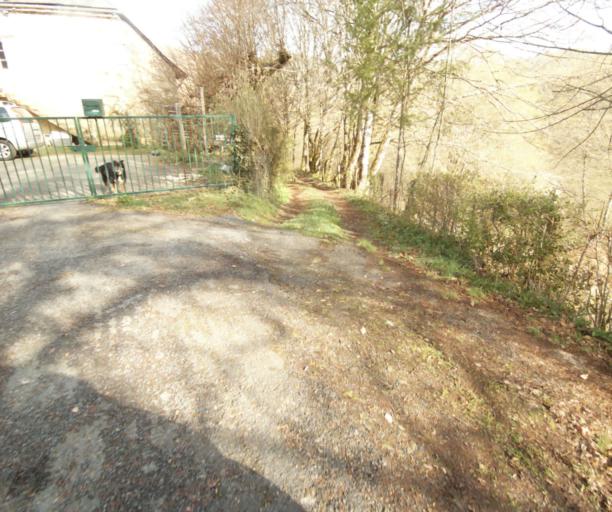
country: FR
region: Limousin
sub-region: Departement de la Correze
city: Naves
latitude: 45.3363
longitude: 1.8179
